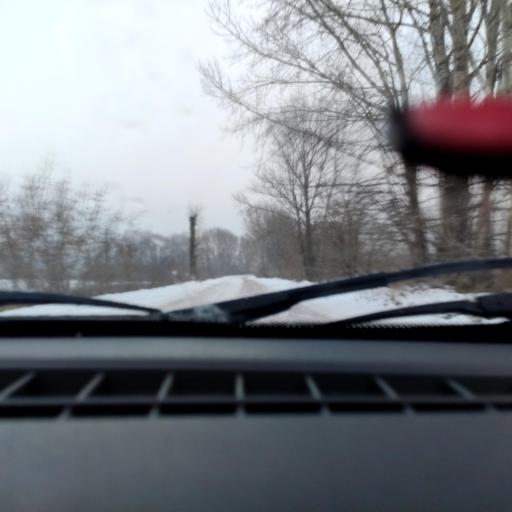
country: RU
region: Bashkortostan
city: Blagoveshchensk
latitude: 54.9113
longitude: 56.0017
